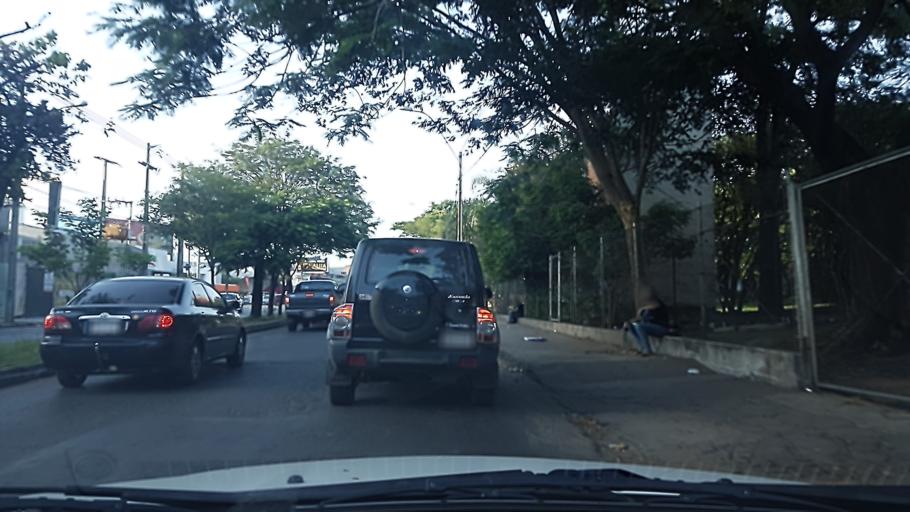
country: PY
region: Asuncion
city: Asuncion
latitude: -25.2854
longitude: -57.5719
